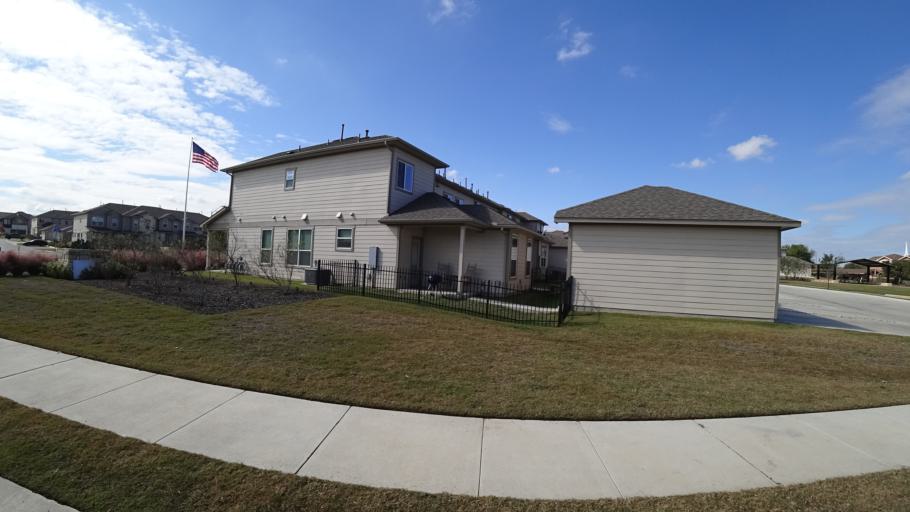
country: US
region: Texas
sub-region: Travis County
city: Windemere
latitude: 30.4515
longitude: -97.6358
